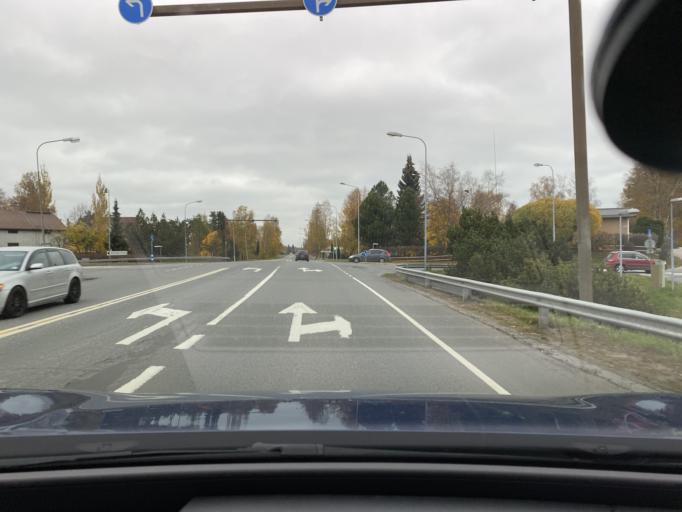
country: FI
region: Varsinais-Suomi
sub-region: Vakka-Suomi
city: Laitila
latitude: 60.8755
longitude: 21.7005
